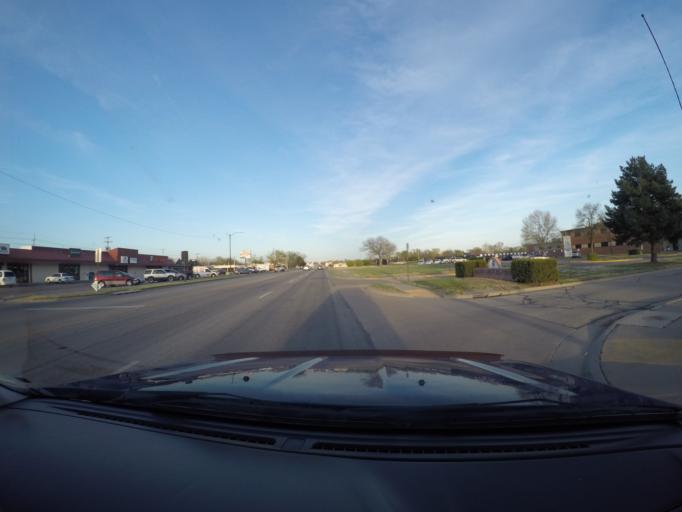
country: US
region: Kansas
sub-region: Saline County
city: Salina
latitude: 38.8271
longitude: -97.6021
